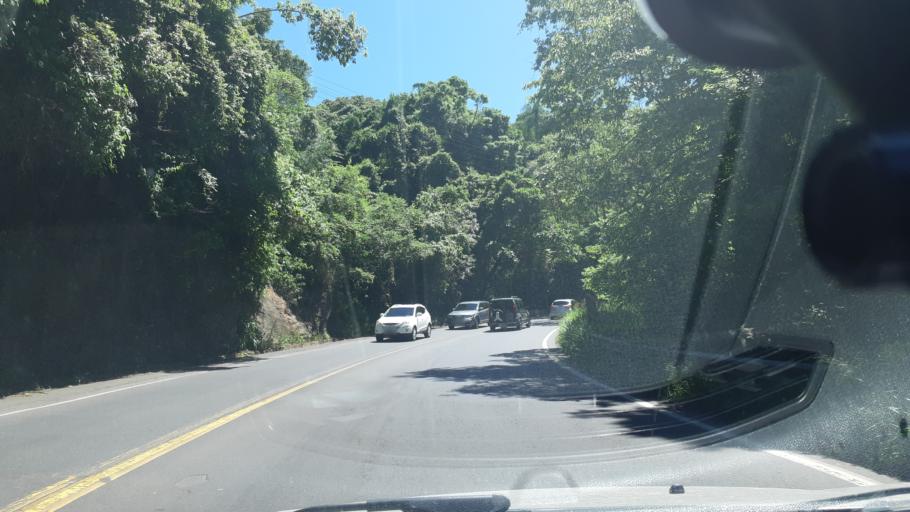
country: BR
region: Rio Grande do Sul
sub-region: Estancia Velha
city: Estancia Velha
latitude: -29.6293
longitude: -51.1437
